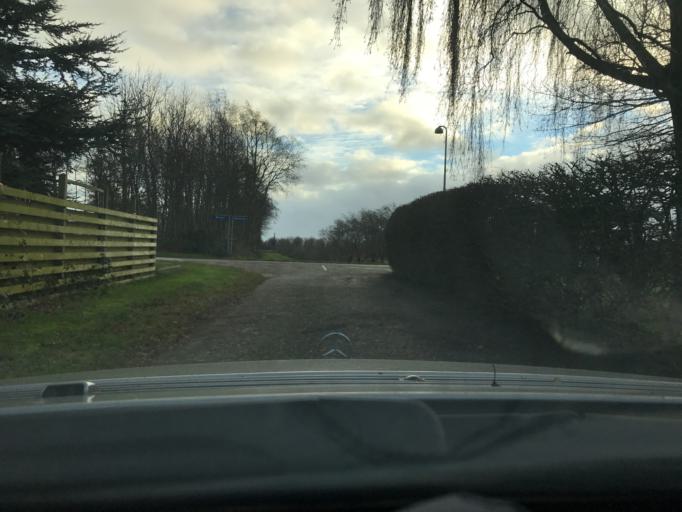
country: DK
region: South Denmark
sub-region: Sonderborg Kommune
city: Nordborg
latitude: 55.0497
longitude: 9.6798
